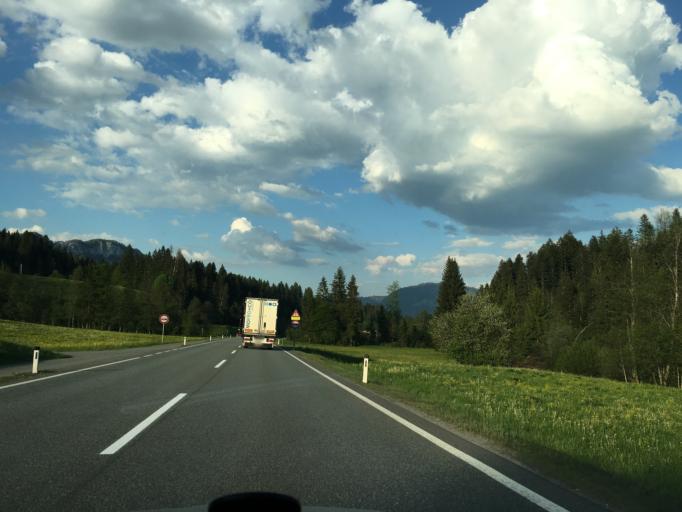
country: AT
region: Tyrol
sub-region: Politischer Bezirk Kitzbuhel
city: Oberndorf in Tirol
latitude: 47.5197
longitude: 12.3669
